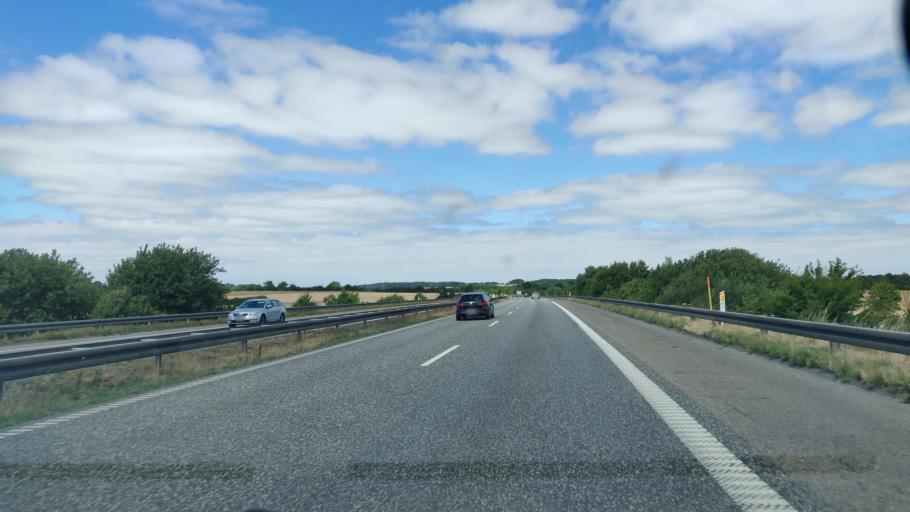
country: DK
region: South Denmark
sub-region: Fredericia Kommune
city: Taulov
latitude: 55.5786
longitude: 9.6136
